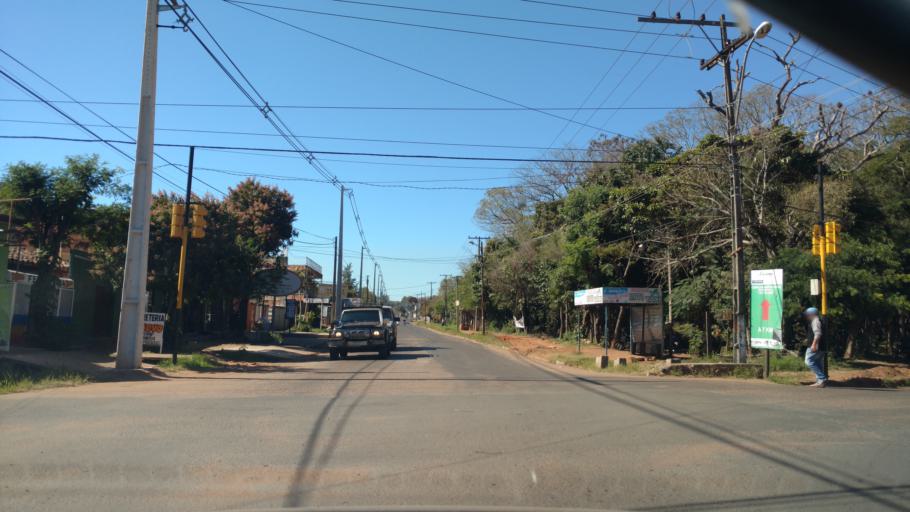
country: PY
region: Central
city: Itaugua
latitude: -25.3974
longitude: -57.3468
